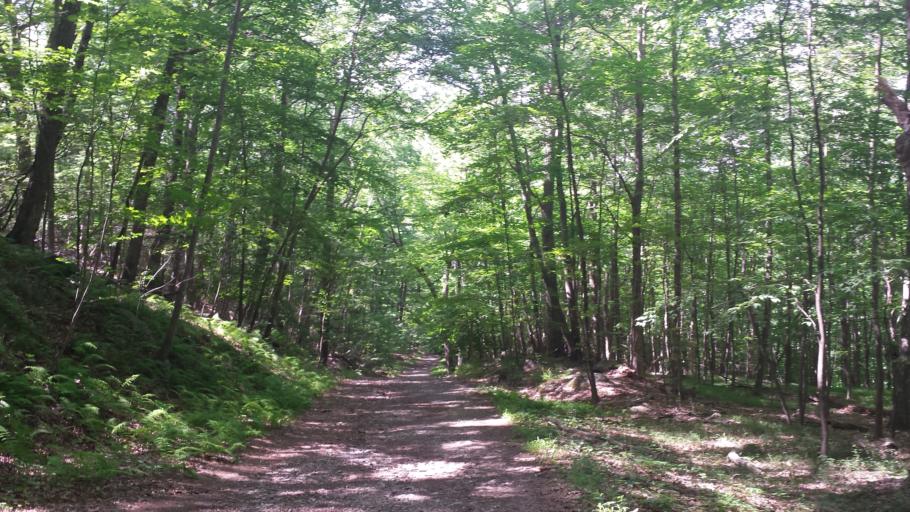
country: US
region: New York
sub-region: Westchester County
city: Pound Ridge
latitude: 41.2431
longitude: -73.5886
